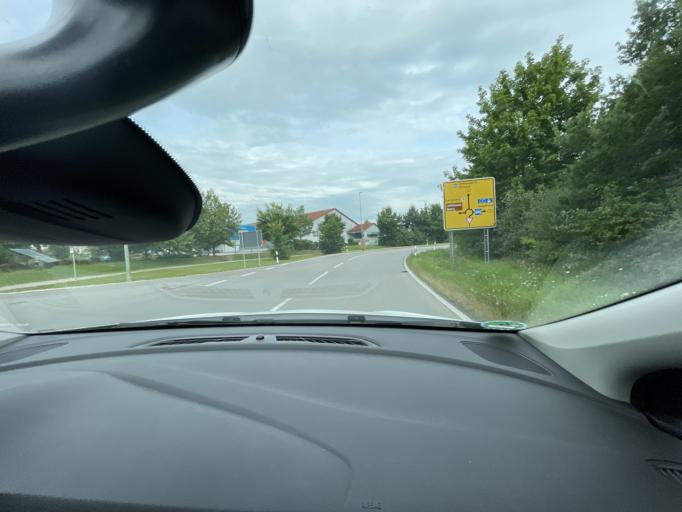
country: DE
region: Bavaria
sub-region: Swabia
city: Langweid
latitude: 48.4847
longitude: 10.8608
